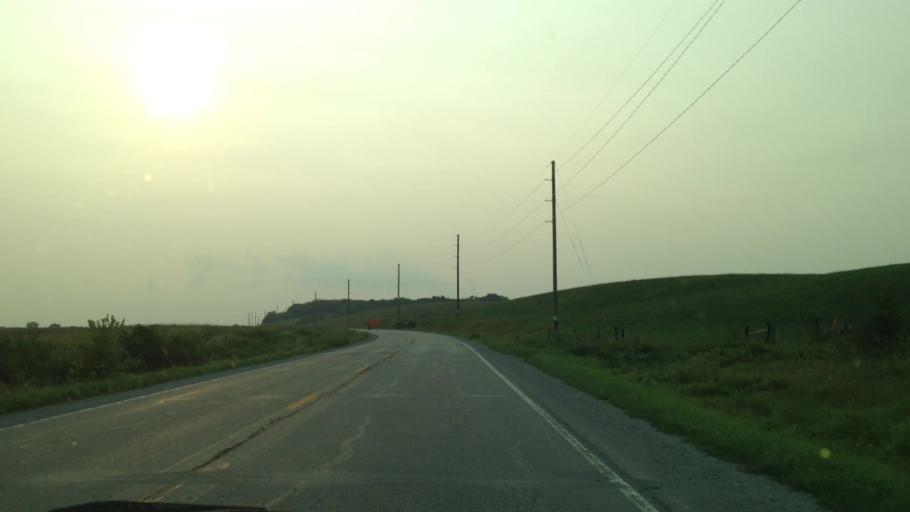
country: US
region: Iowa
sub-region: Benton County
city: Walford
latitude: 41.7969
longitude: -91.9152
